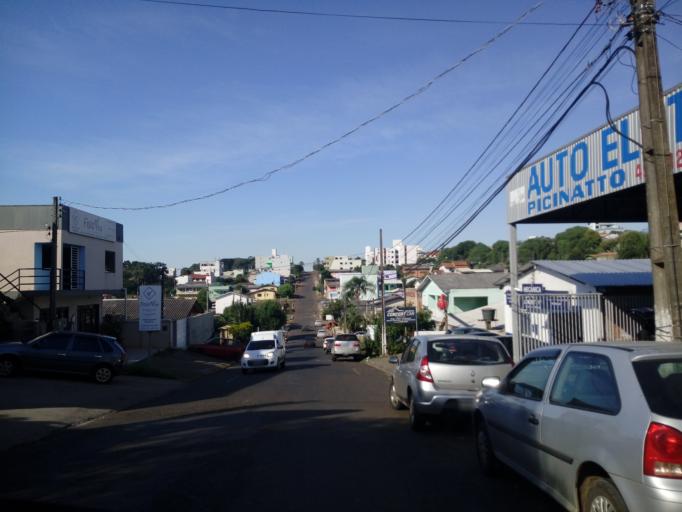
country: BR
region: Santa Catarina
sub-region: Chapeco
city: Chapeco
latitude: -27.0964
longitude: -52.6694
